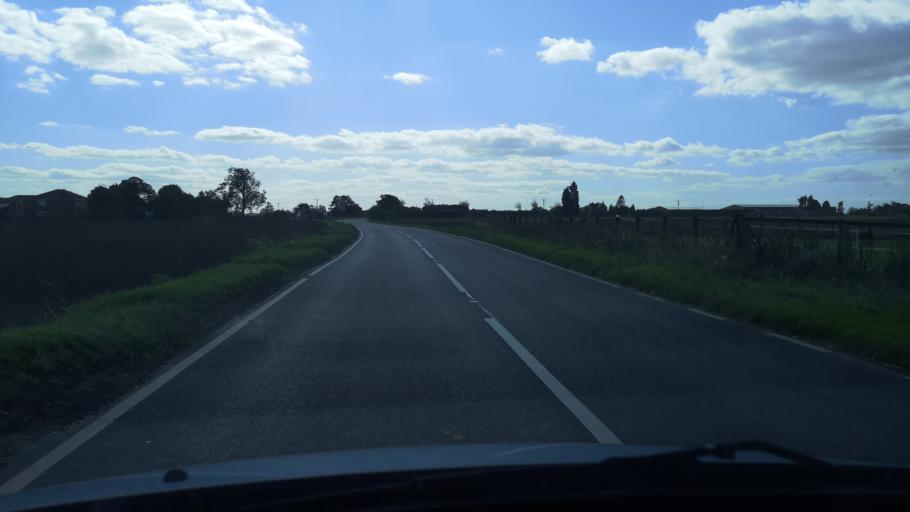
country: GB
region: England
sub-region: North Lincolnshire
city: Eastoft
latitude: 53.6328
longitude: -0.7904
